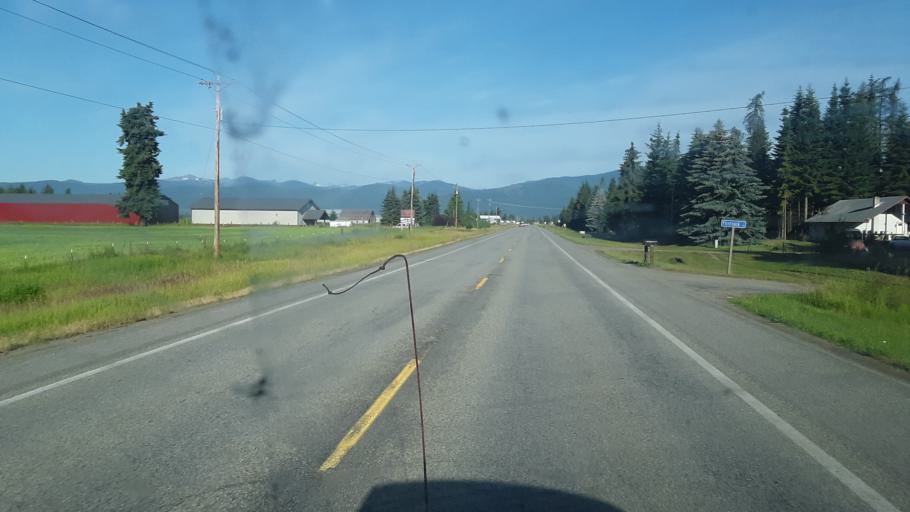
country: US
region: Idaho
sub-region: Boundary County
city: Bonners Ferry
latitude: 48.7314
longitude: -116.2796
